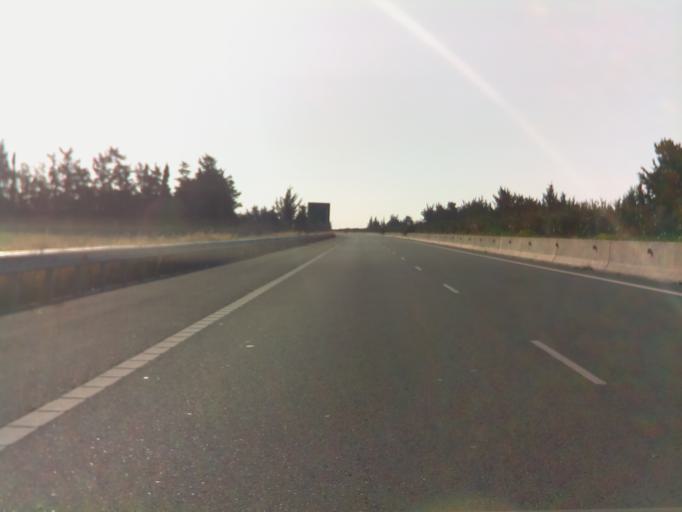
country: CY
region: Limassol
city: Pissouri
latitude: 34.6959
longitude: 32.5736
